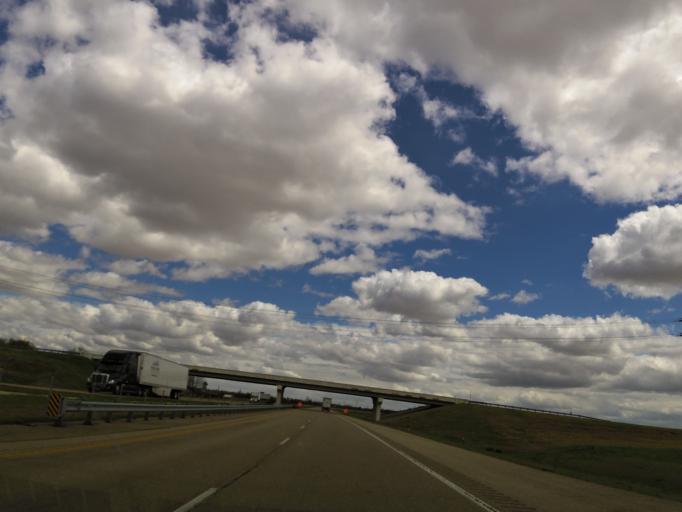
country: US
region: Arkansas
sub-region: Poinsett County
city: Marked Tree
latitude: 35.5198
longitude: -90.4140
